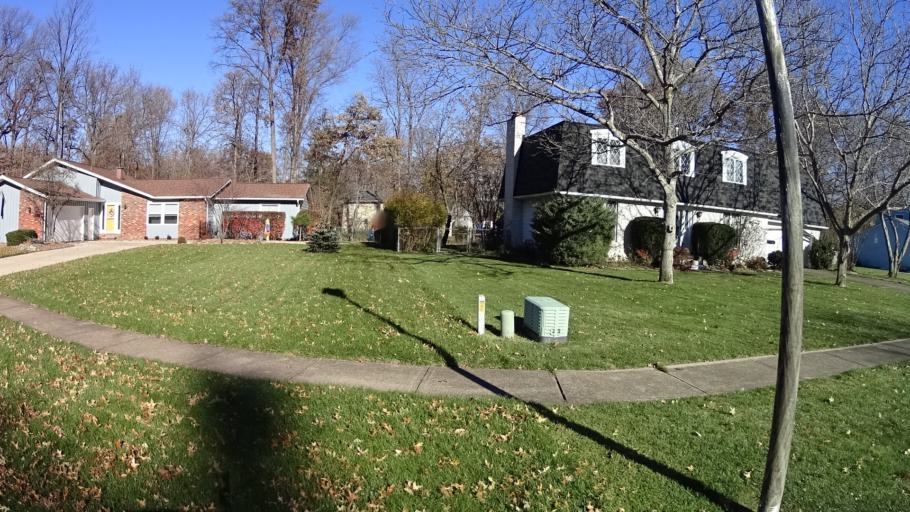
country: US
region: Ohio
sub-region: Lorain County
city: Avon Lake
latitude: 41.5000
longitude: -82.0206
